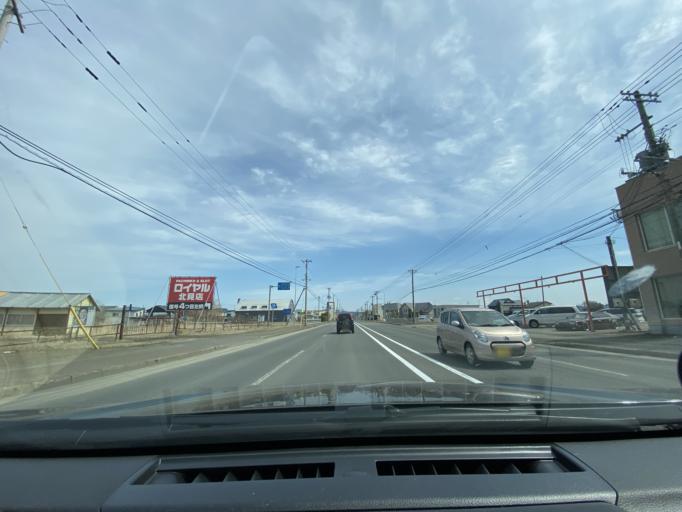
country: JP
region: Hokkaido
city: Kitami
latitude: 43.8005
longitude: 143.8249
